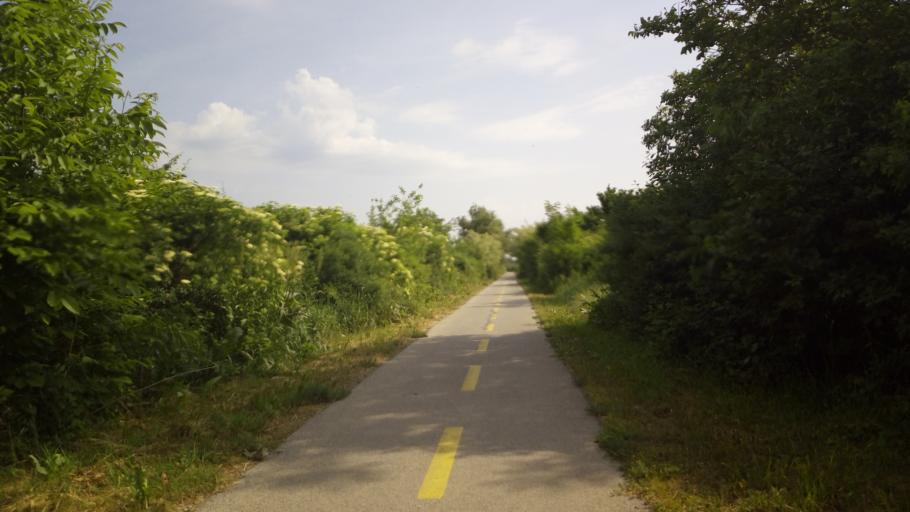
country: HU
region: Baranya
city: Pellerd
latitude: 46.0499
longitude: 18.1950
